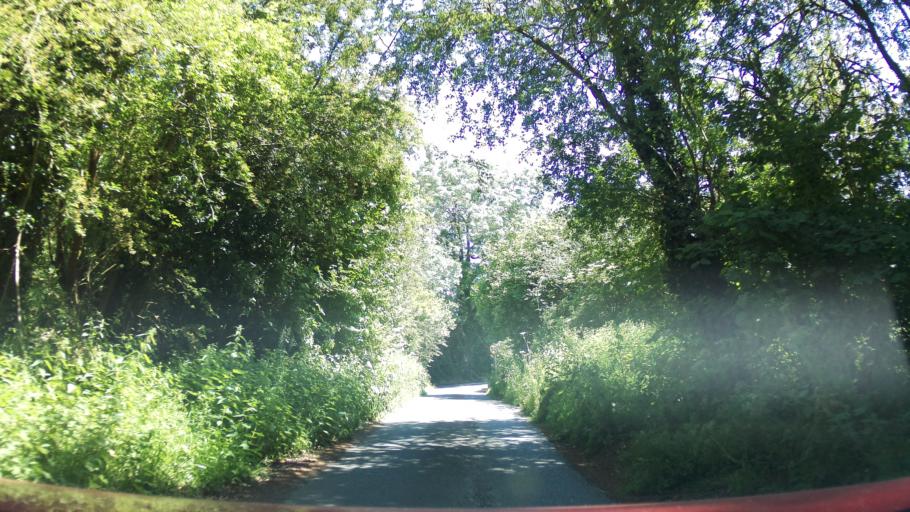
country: GB
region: England
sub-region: Wiltshire
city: Chippenham
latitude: 51.4826
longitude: -2.1084
